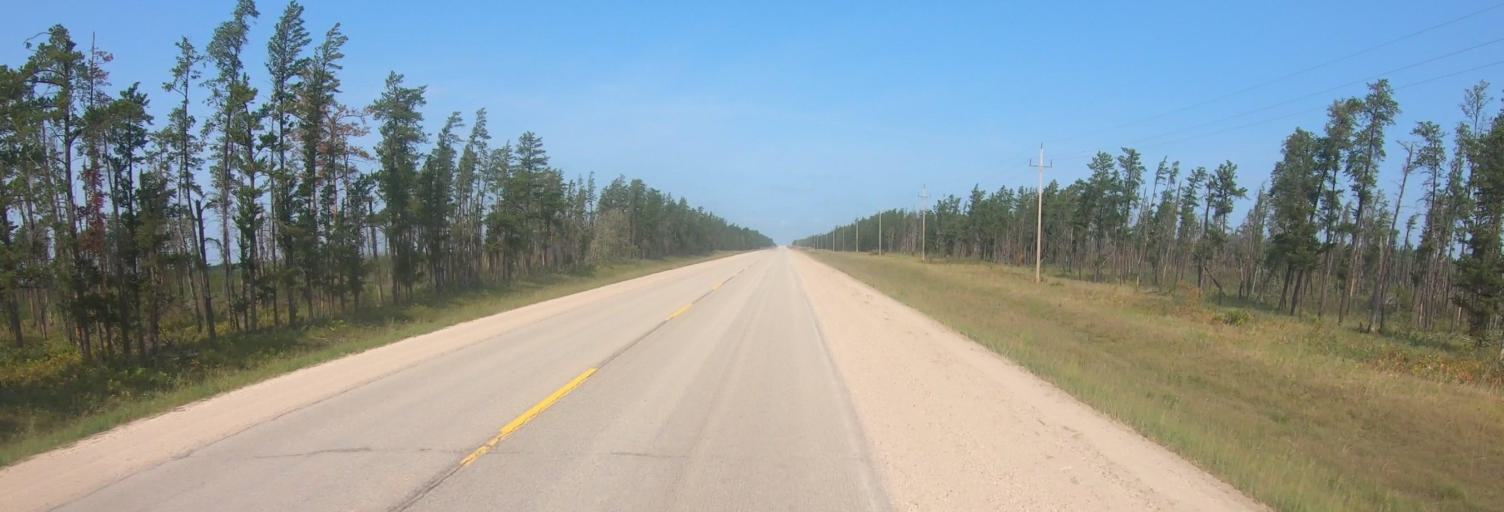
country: US
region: Minnesota
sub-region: Roseau County
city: Roseau
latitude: 49.1243
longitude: -96.0644
